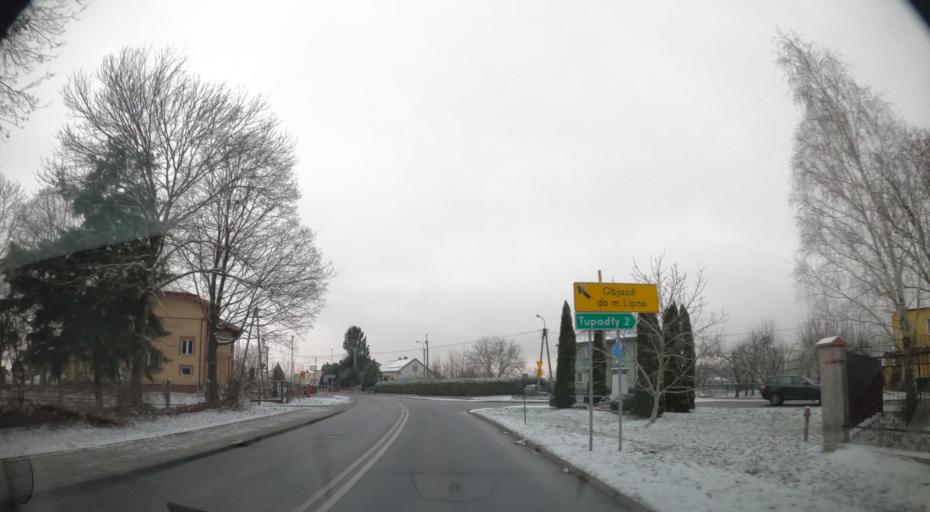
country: PL
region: Kujawsko-Pomorskie
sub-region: Powiat lipnowski
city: Wielgie
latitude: 52.7383
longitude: 19.2739
